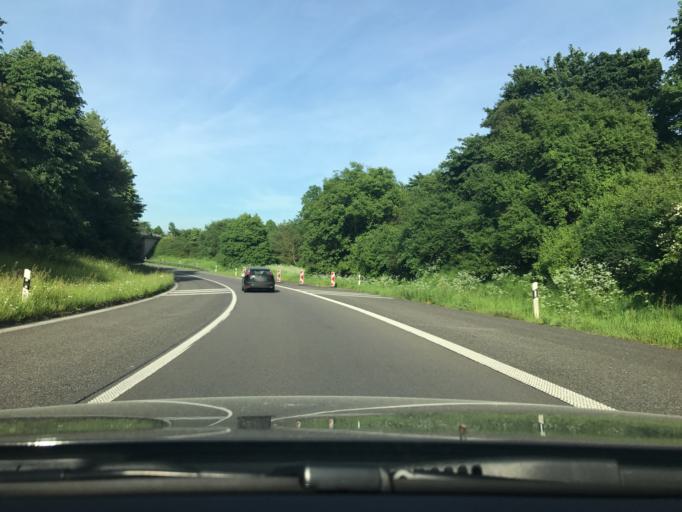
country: DE
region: North Rhine-Westphalia
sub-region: Regierungsbezirk Dusseldorf
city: Willich
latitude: 51.2873
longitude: 6.5234
